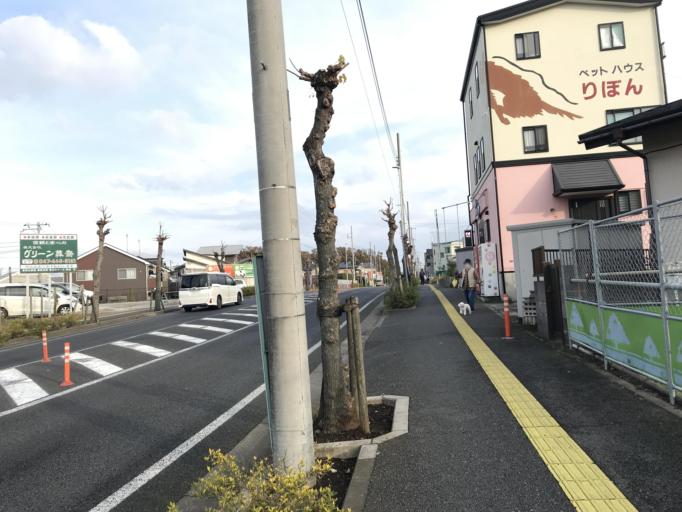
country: JP
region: Chiba
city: Funabashi
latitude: 35.7624
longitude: 140.0012
